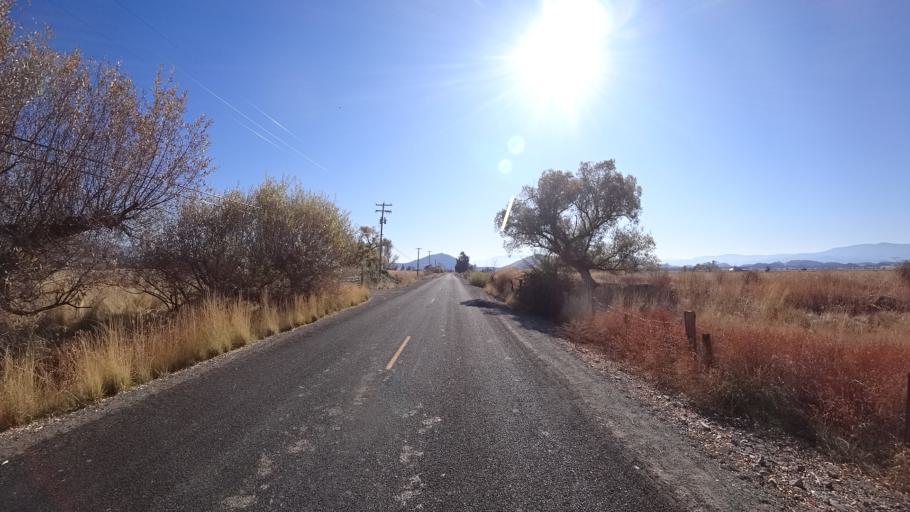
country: US
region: California
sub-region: Siskiyou County
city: Montague
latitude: 41.7171
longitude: -122.3892
